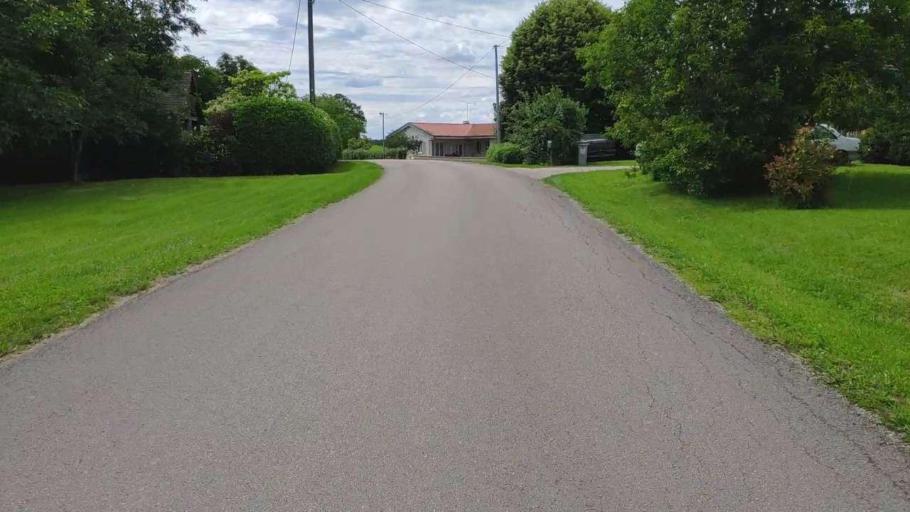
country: FR
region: Franche-Comte
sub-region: Departement du Jura
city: Chaussin
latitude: 46.8712
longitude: 5.4159
